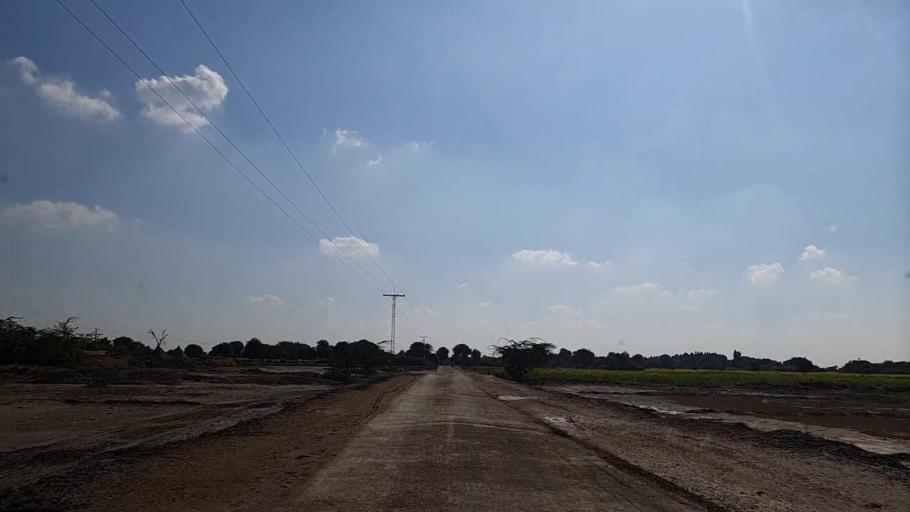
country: PK
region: Sindh
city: Pithoro
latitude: 25.6581
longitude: 69.4493
